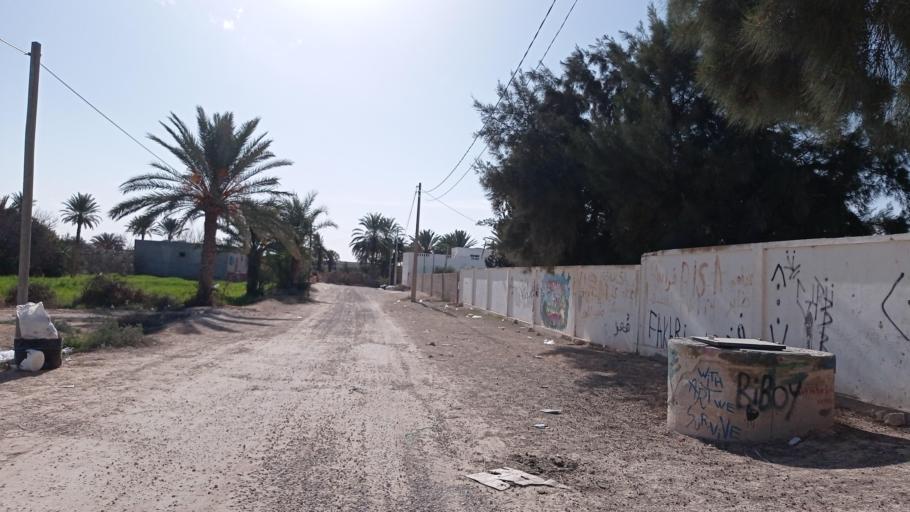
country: TN
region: Qabis
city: Gabes
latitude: 33.8308
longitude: 10.1118
